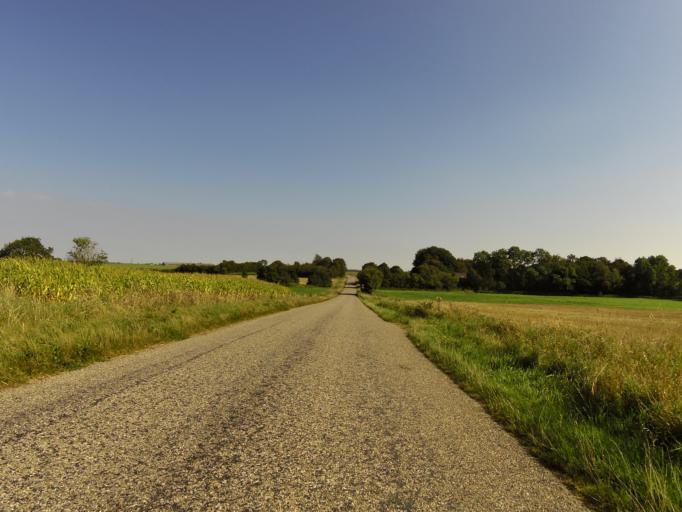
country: DK
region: South Denmark
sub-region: Vejen Kommune
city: Rodding
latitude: 55.3327
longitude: 9.1284
